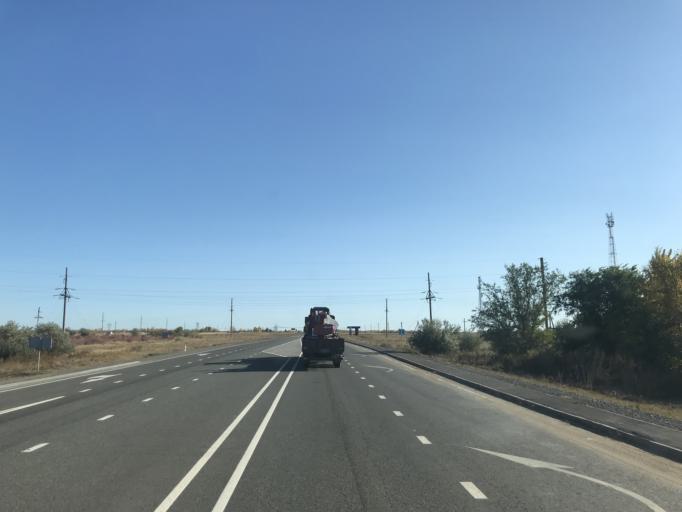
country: KZ
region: Pavlodar
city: Koktobe
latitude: 51.9255
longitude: 77.3351
